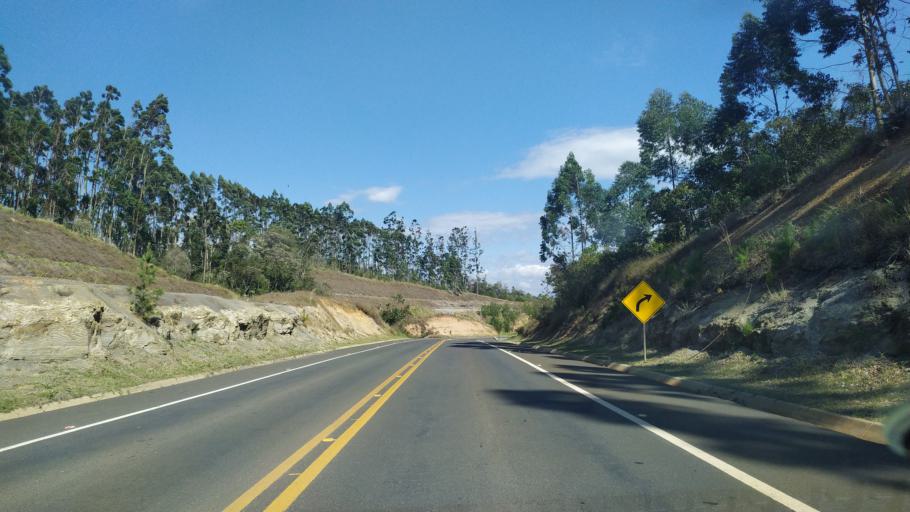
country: BR
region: Parana
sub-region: Ortigueira
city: Ortigueira
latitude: -24.2920
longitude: -50.8173
